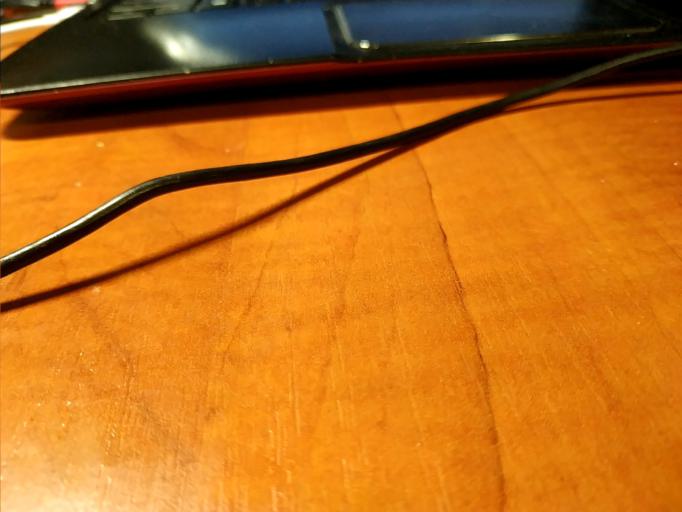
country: RU
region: Tverskaya
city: Rameshki
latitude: 57.2161
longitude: 36.0916
